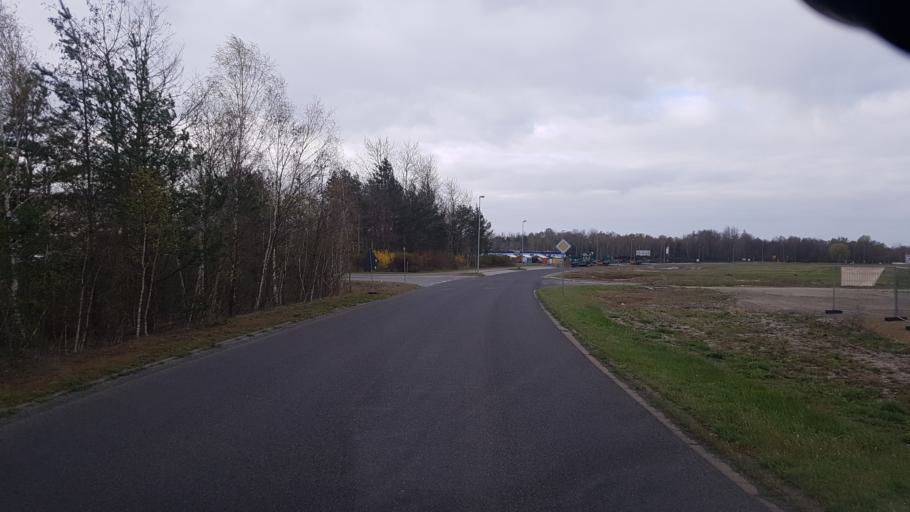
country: DE
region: Brandenburg
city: Lauchhammer
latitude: 51.4811
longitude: 13.7938
